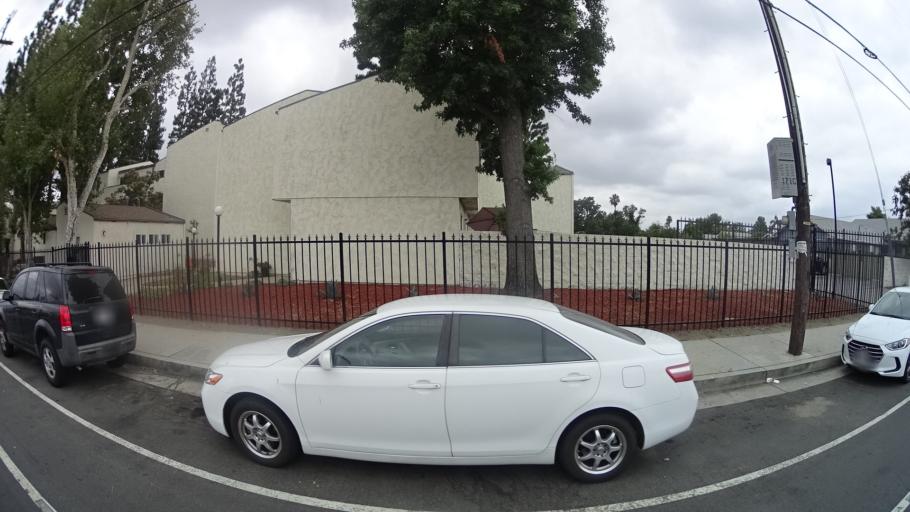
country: US
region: California
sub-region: Los Angeles County
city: San Fernando
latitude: 34.2366
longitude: -118.4414
